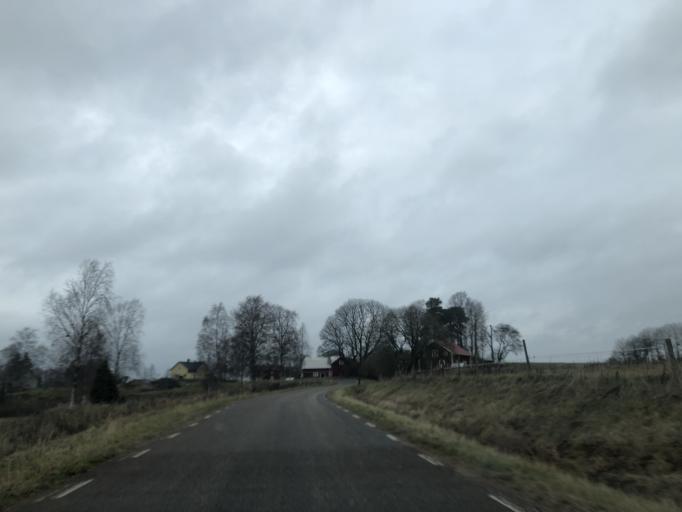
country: SE
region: Vaestra Goetaland
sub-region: Ulricehamns Kommun
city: Ulricehamn
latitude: 57.8768
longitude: 13.5378
